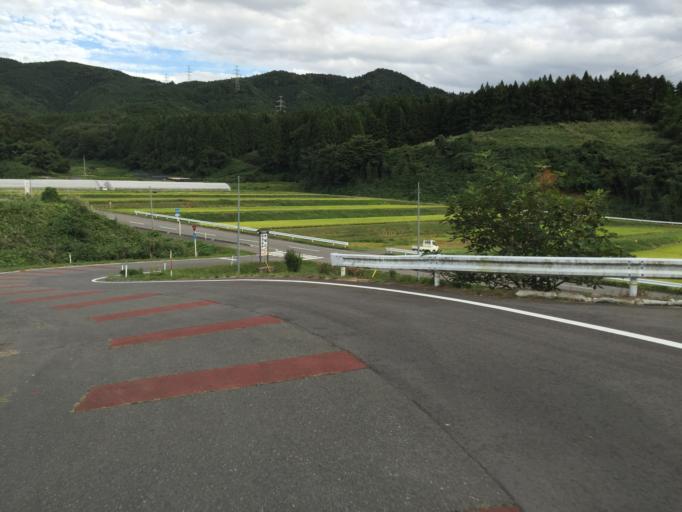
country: JP
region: Fukushima
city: Nihommatsu
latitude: 37.6118
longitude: 140.5853
